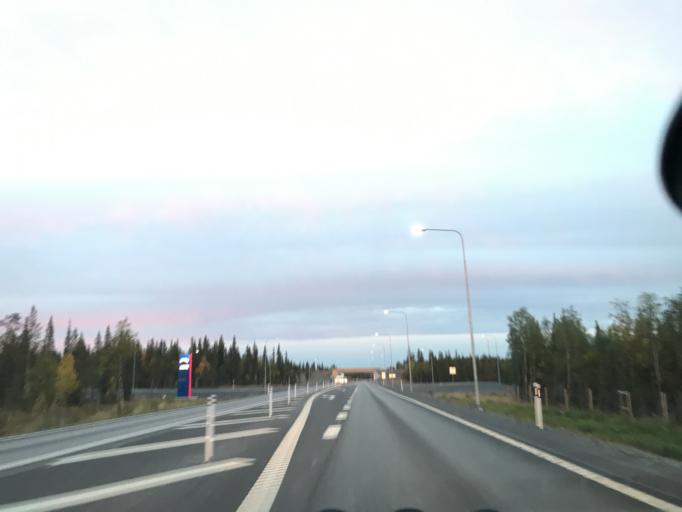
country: SE
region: Norrbotten
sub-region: Gallivare Kommun
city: Malmberget
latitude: 67.6949
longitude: 20.8054
